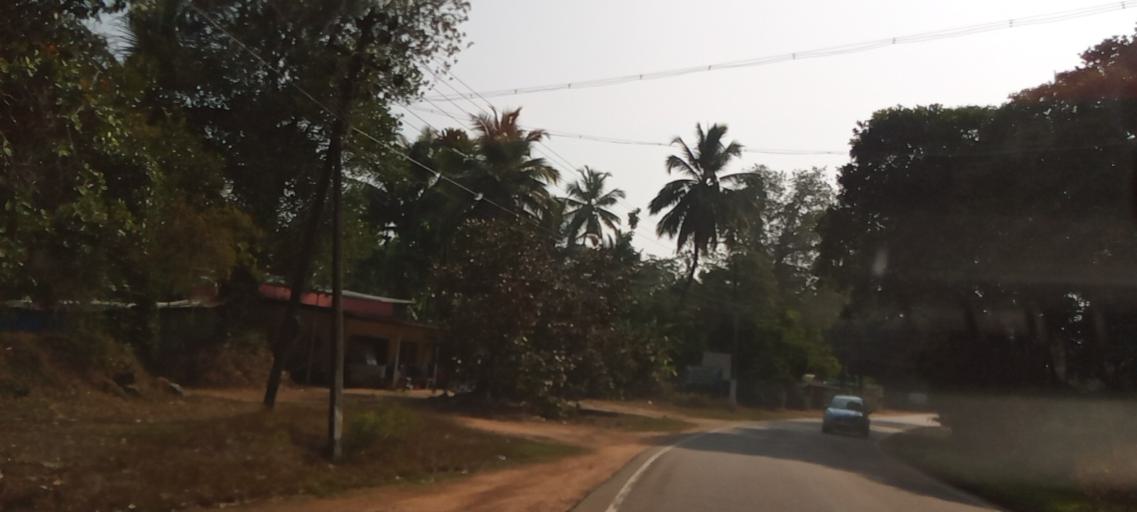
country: IN
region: Karnataka
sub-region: Udupi
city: Coondapoor
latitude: 13.5164
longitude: 74.7894
